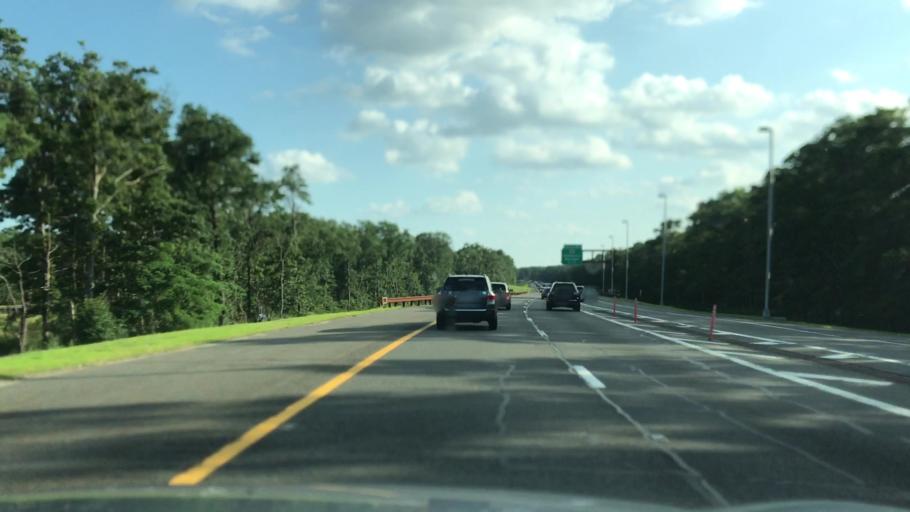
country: US
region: New Jersey
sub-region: Ocean County
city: Barnegat
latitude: 39.7724
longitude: -74.2456
